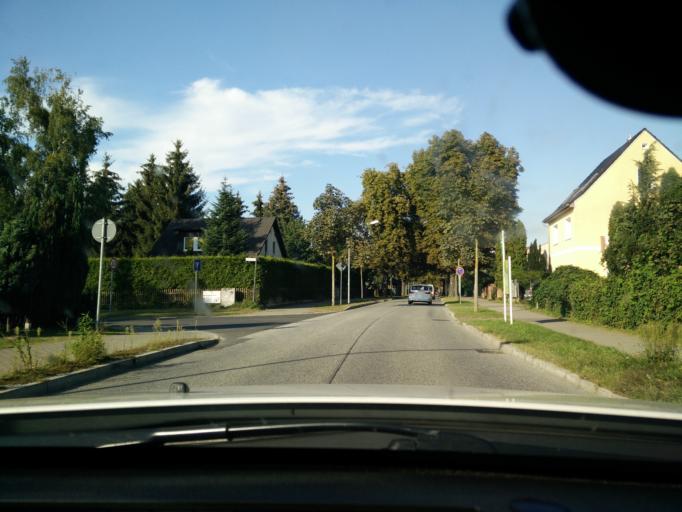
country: DE
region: Brandenburg
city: Dallgow-Doeberitz
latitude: 52.5501
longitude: 13.0684
